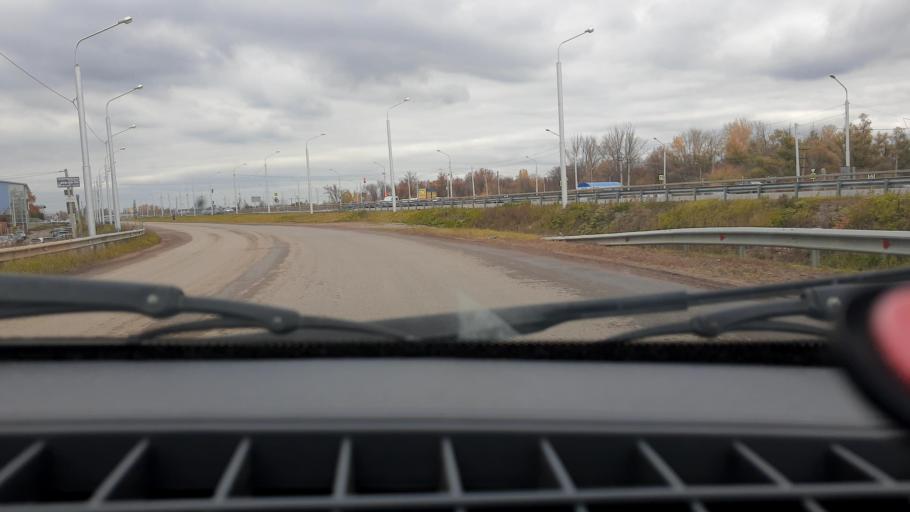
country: RU
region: Bashkortostan
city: Ufa
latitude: 54.7676
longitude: 55.9540
